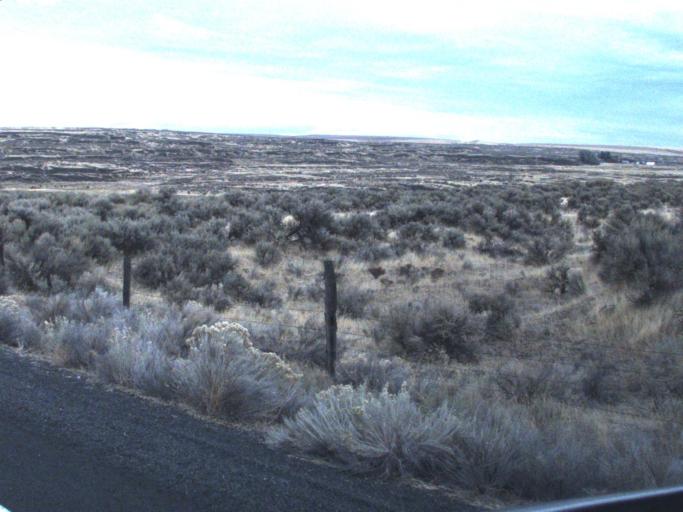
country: US
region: Washington
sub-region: Adams County
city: Ritzville
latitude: 47.4612
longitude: -118.7609
